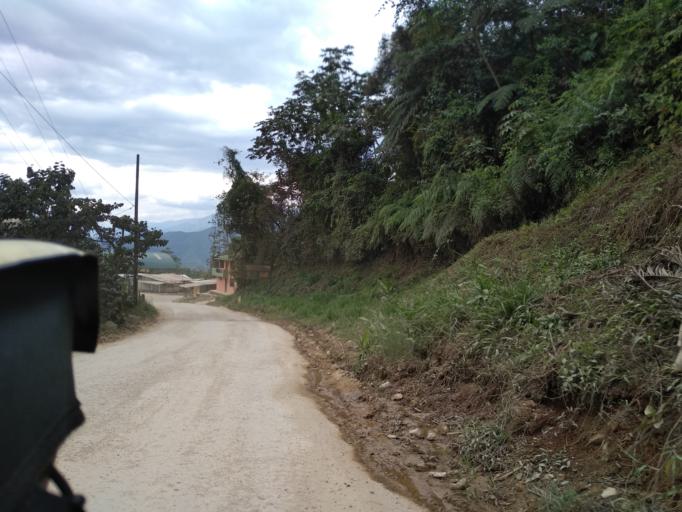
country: PE
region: Cajamarca
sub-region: Provincia de San Ignacio
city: Namballe
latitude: -4.8626
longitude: -79.1263
